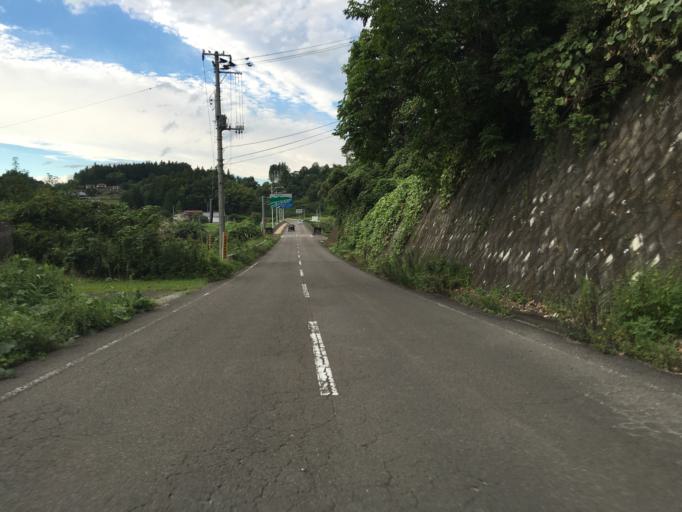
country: JP
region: Fukushima
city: Nihommatsu
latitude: 37.5898
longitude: 140.4983
